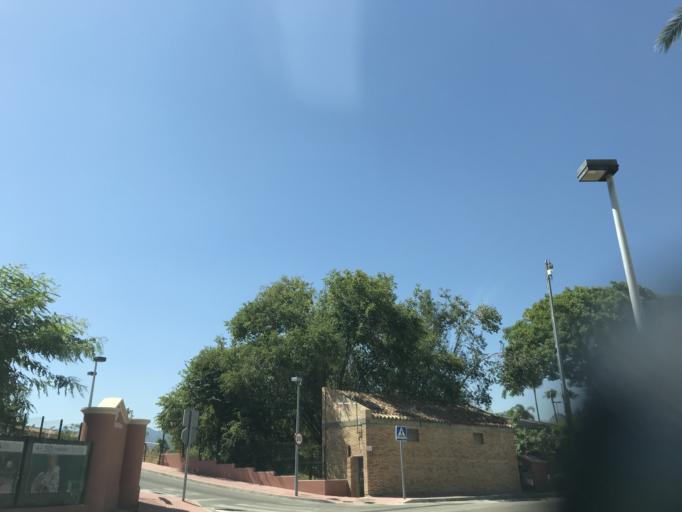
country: ES
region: Andalusia
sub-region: Provincia de Malaga
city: Benahavis
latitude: 36.4591
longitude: -5.0475
